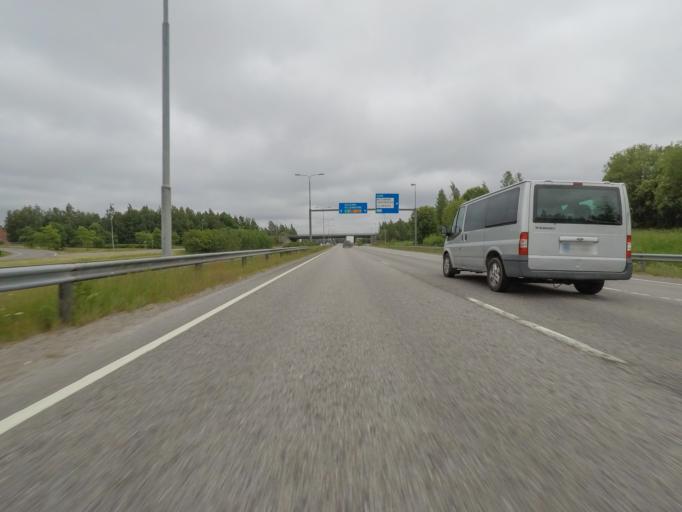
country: FI
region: Varsinais-Suomi
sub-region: Turku
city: Turku
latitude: 60.4883
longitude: 22.3179
